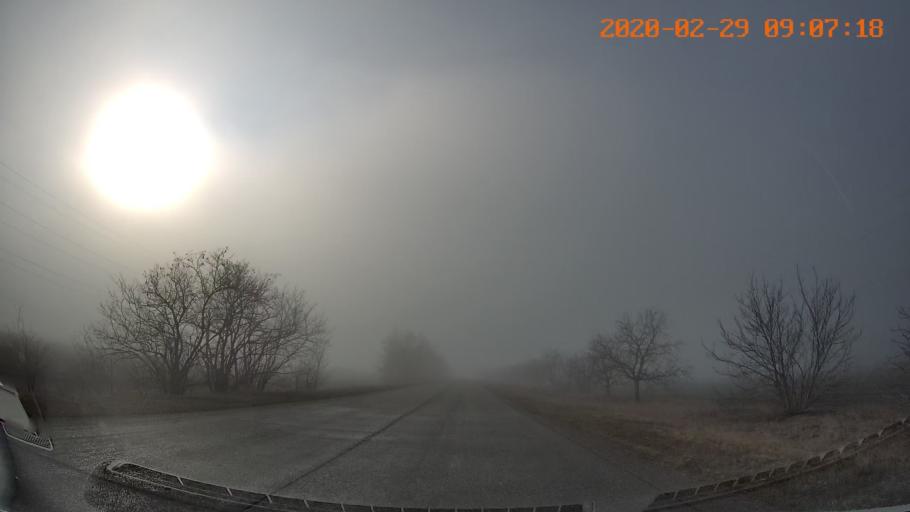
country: MD
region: Telenesti
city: Tiraspolul Nou
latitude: 46.8638
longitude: 29.7483
